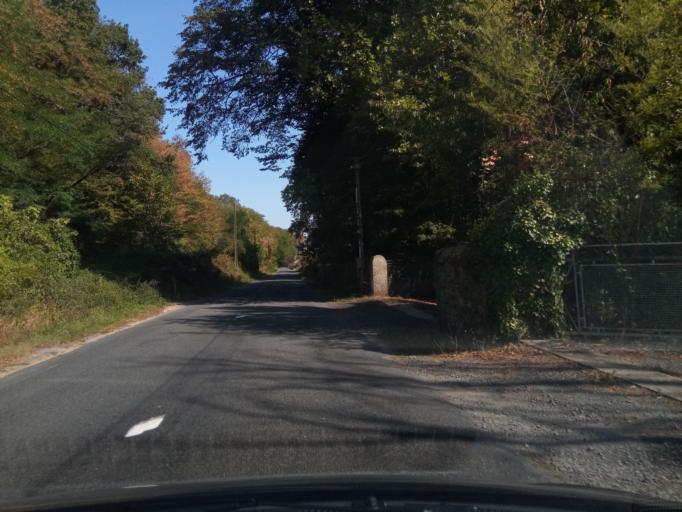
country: FR
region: Poitou-Charentes
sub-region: Departement de la Vienne
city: Saulge
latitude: 46.4022
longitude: 0.8742
